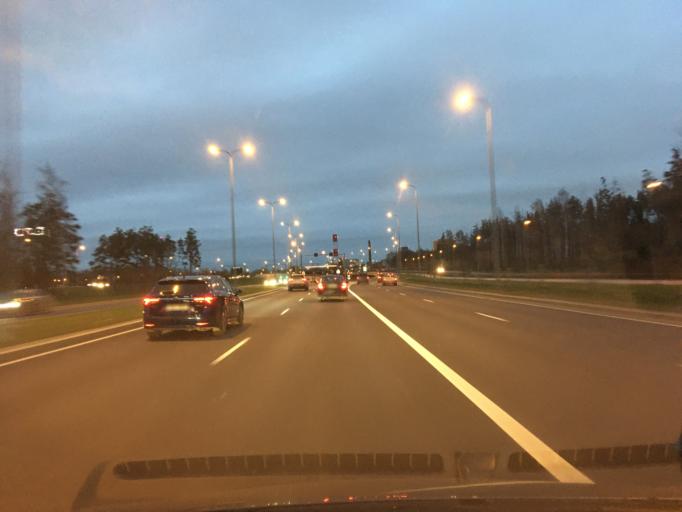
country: EE
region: Harju
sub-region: Tallinna linn
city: Tallinn
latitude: 59.4162
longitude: 24.7633
